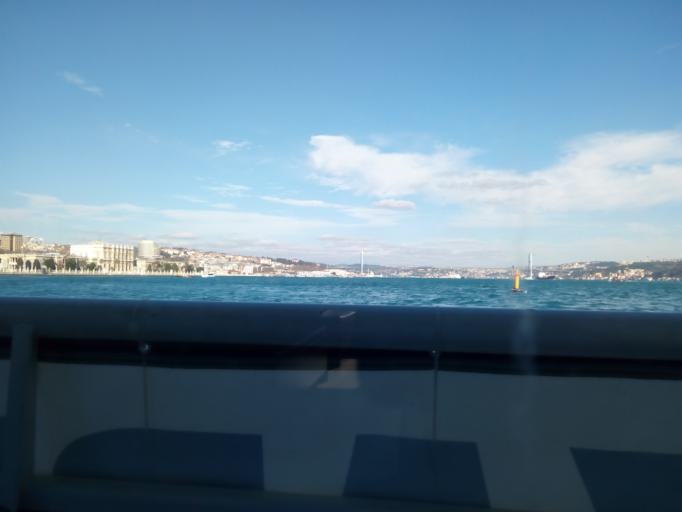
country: TR
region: Istanbul
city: Eminoenue
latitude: 41.0335
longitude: 28.9955
